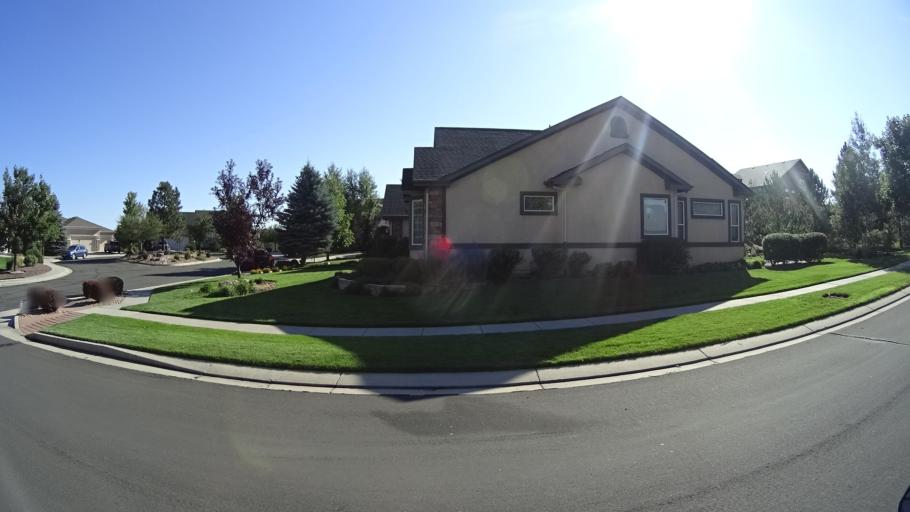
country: US
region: Colorado
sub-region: El Paso County
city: Black Forest
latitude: 38.9790
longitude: -104.7659
